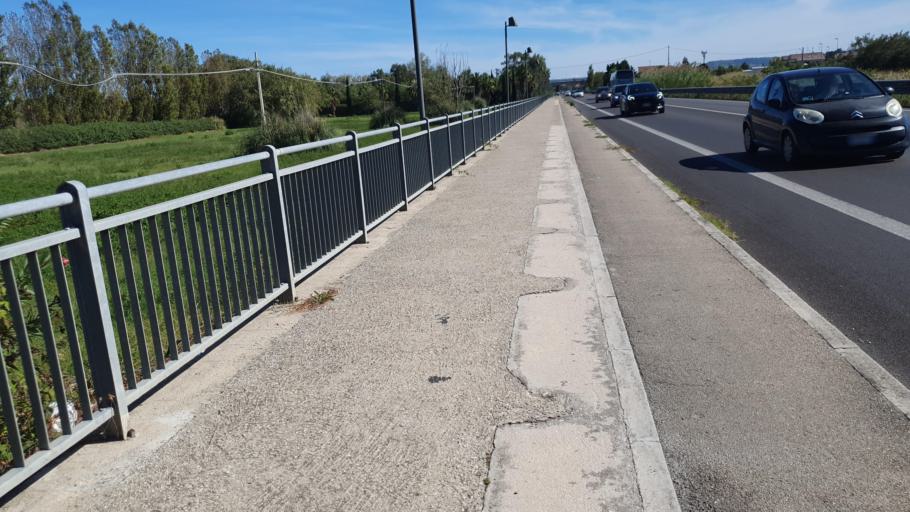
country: IT
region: Abruzzo
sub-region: Provincia di Chieti
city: Salvo Marina
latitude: 42.0658
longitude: 14.7776
